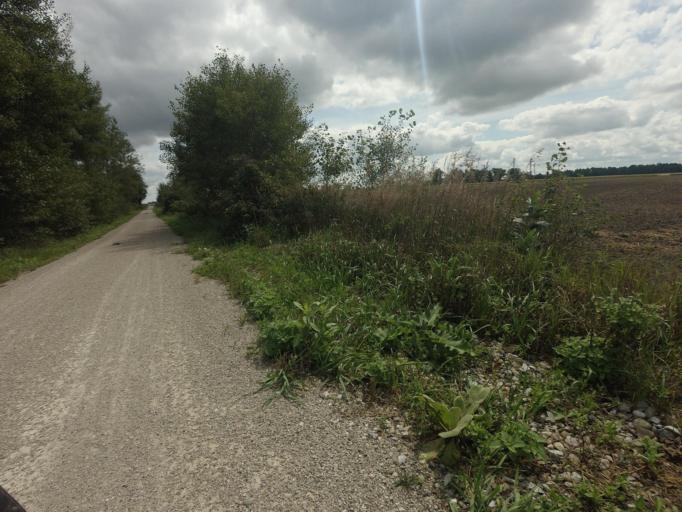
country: CA
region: Ontario
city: North Perth
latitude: 43.5652
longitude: -81.0217
